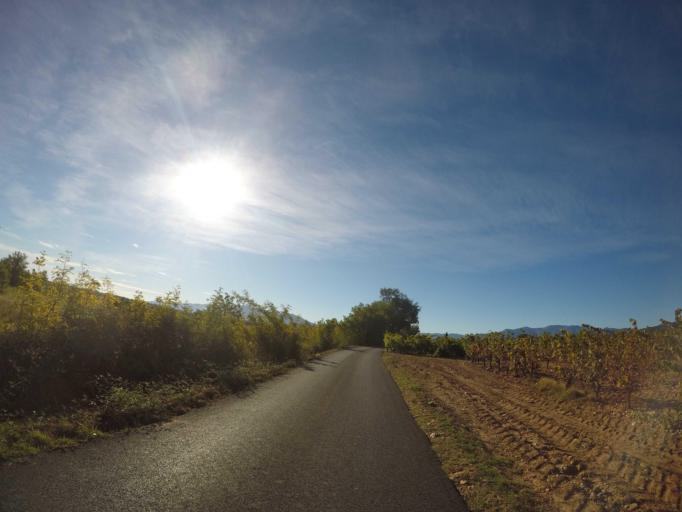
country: FR
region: Languedoc-Roussillon
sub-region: Departement des Pyrenees-Orientales
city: Llupia
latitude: 42.5961
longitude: 2.7635
